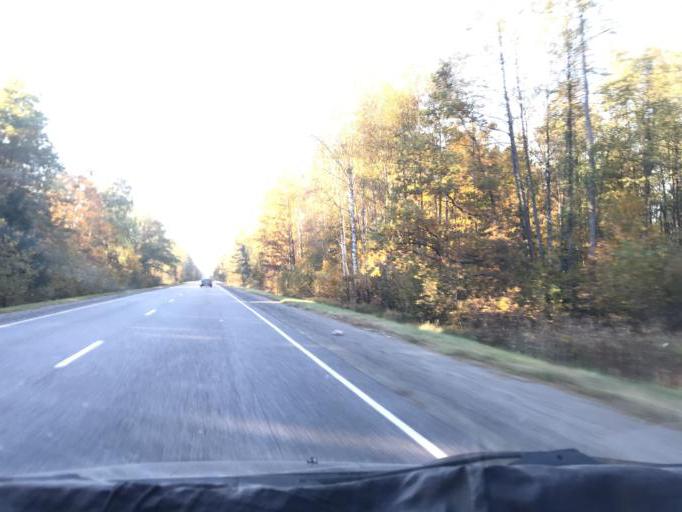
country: BY
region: Gomel
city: Pyetrykaw
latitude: 52.2610
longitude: 28.3259
